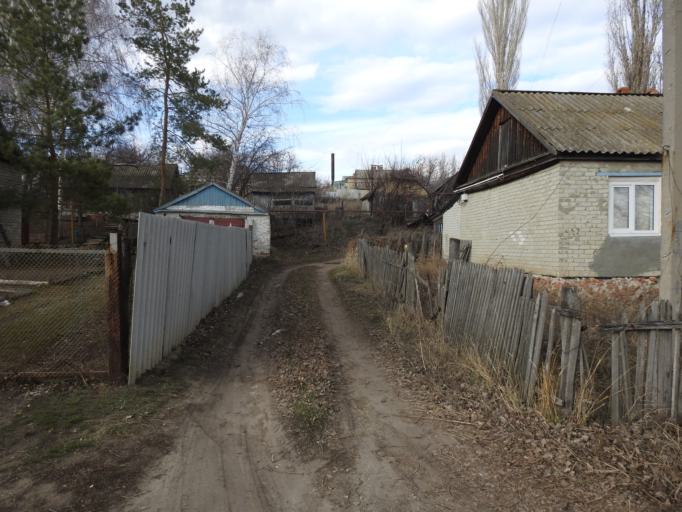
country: RU
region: Saratov
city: Sokolovyy
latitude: 51.3851
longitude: 45.8128
